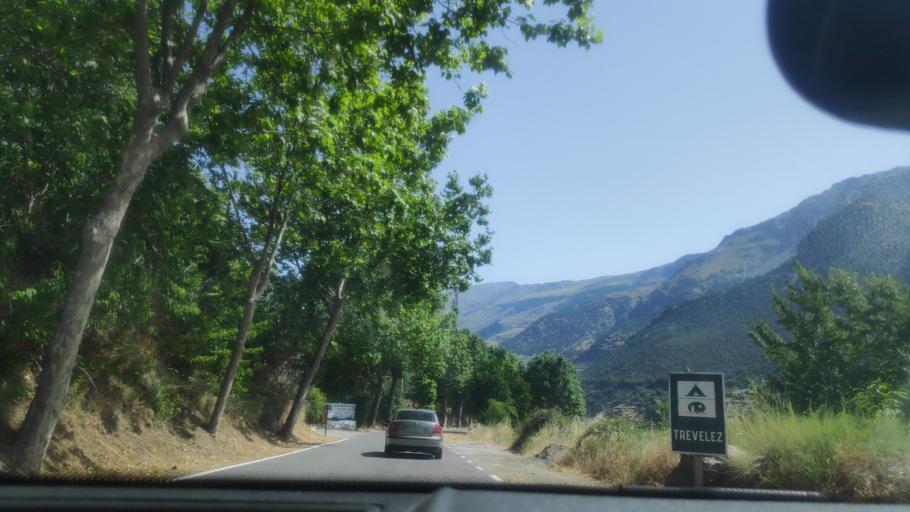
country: ES
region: Andalusia
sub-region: Provincia de Granada
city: Trevelez
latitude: 36.9914
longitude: -3.2708
